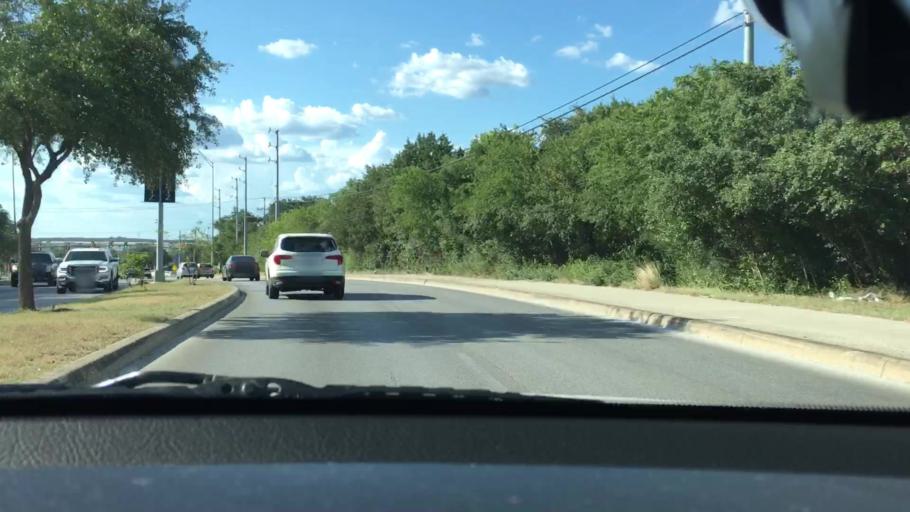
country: US
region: Texas
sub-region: Bexar County
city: Selma
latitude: 29.5913
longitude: -98.2891
